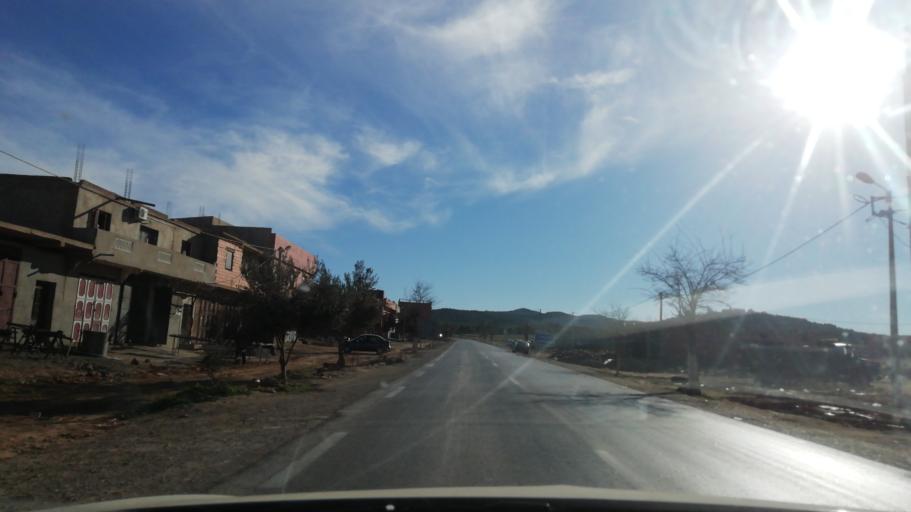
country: DZ
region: Tlemcen
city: Sebdou
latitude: 34.6238
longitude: -1.3341
